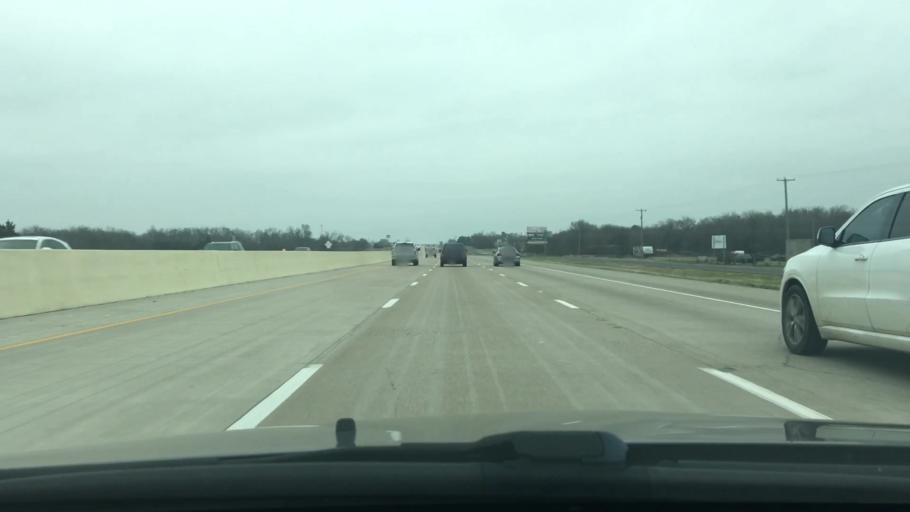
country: US
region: Texas
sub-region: Navarro County
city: Corsicana
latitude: 32.0228
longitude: -96.4400
